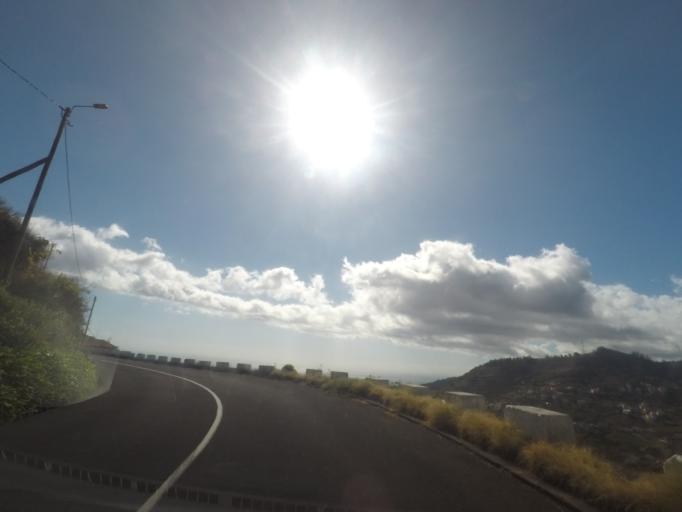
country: PT
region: Madeira
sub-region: Ribeira Brava
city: Campanario
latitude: 32.6684
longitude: -17.0216
